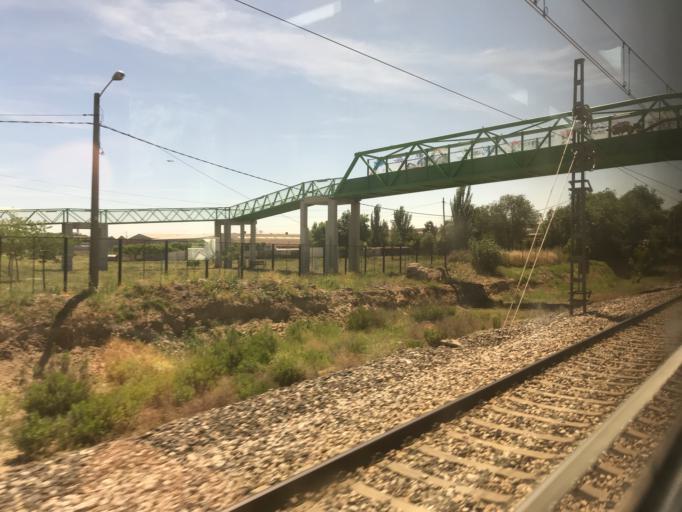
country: ES
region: Madrid
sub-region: Provincia de Madrid
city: Getafe
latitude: 40.3144
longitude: -3.7090
